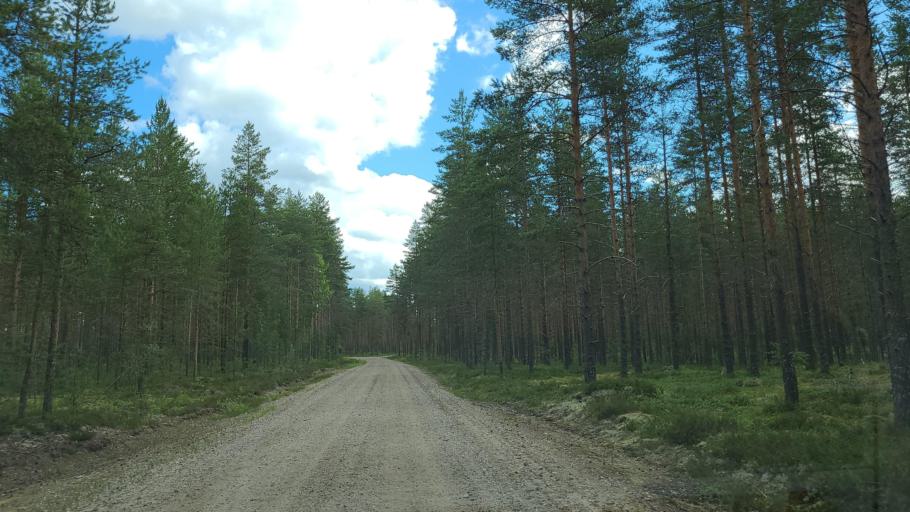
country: FI
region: Northern Savo
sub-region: Koillis-Savo
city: Kaavi
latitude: 63.0529
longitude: 28.8186
